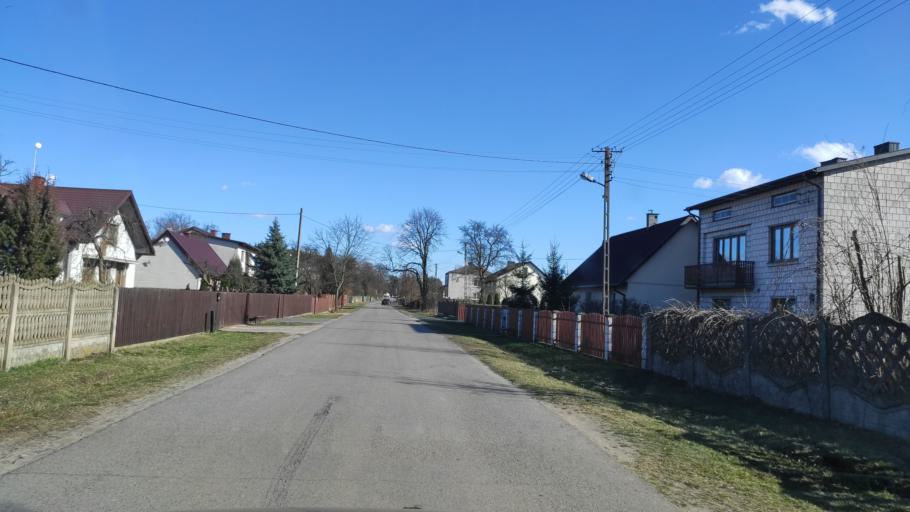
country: PL
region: Masovian Voivodeship
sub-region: Powiat radomski
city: Jastrzebia
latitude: 51.4579
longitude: 21.2647
